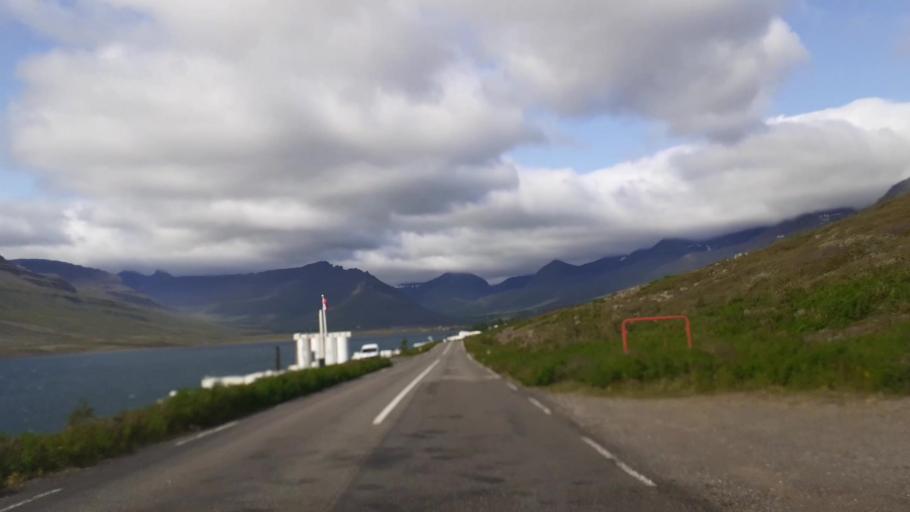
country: IS
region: East
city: Eskifjoerdur
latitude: 64.9237
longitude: -13.9810
